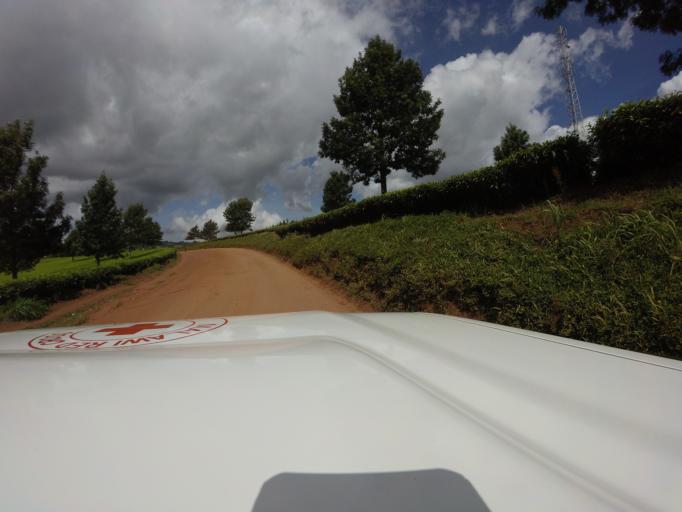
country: MW
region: Southern Region
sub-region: Thyolo District
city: Thyolo
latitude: -15.9902
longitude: 35.0730
